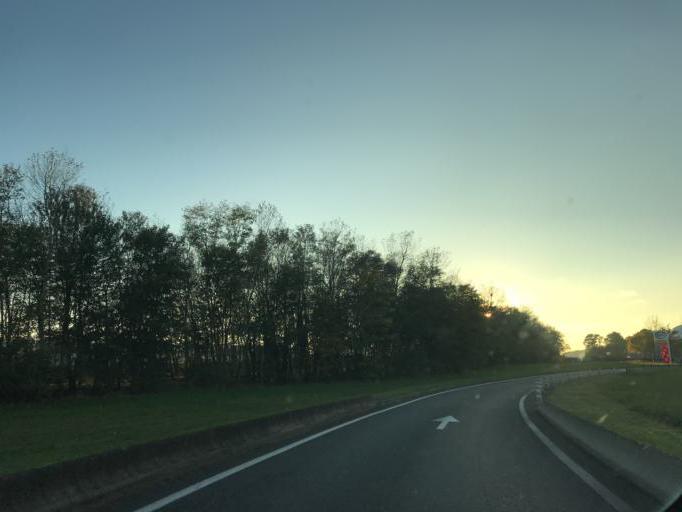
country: FR
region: Bourgogne
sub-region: Departement de l'Yonne
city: Egriselles-le-Bocage
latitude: 48.1656
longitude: 3.1749
